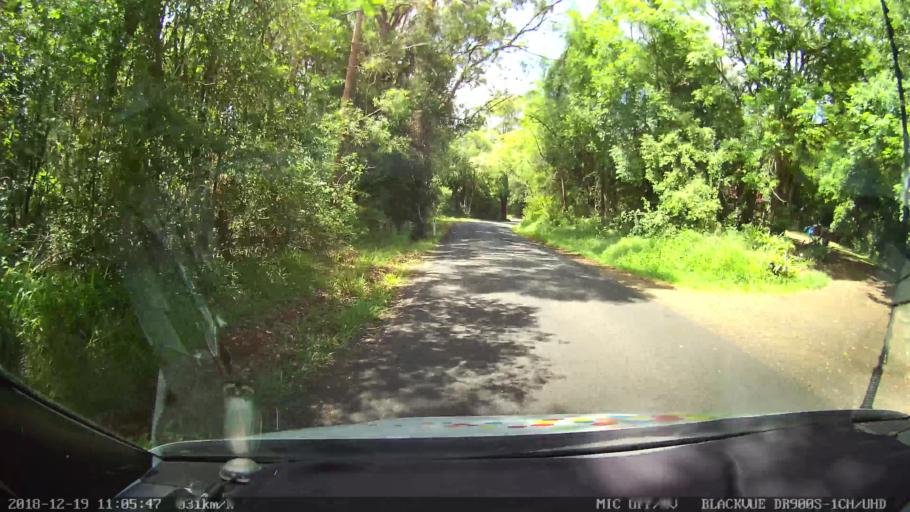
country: AU
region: New South Wales
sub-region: Lismore Municipality
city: Nimbin
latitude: -28.6192
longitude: 153.2651
